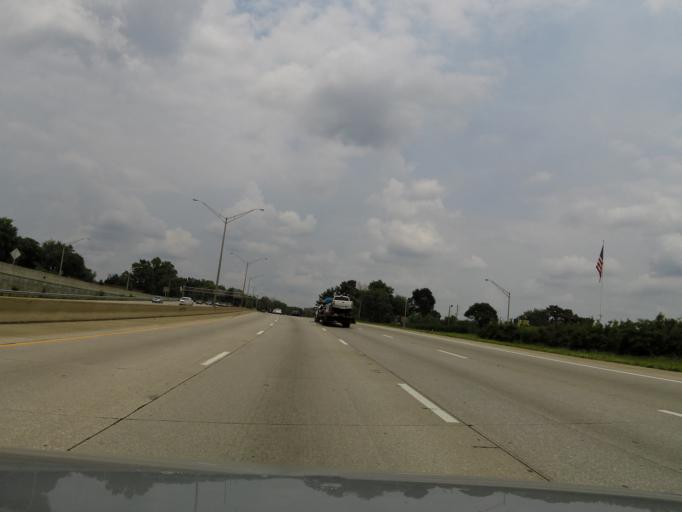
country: US
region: Kentucky
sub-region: Jefferson County
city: Audubon Park
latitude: 38.1960
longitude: -85.7067
